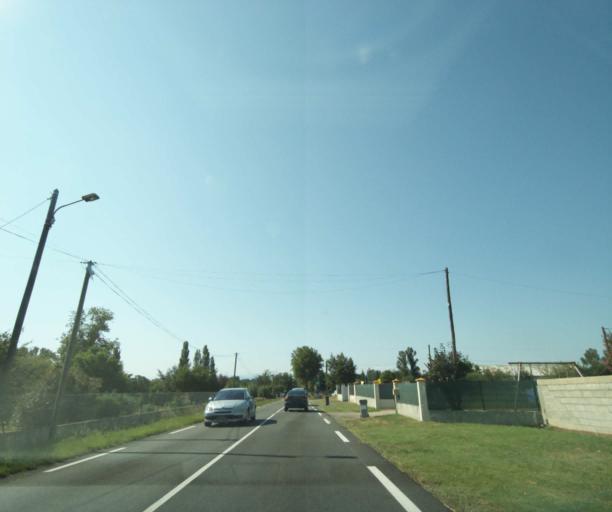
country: FR
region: Midi-Pyrenees
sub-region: Departement de la Haute-Garonne
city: Saint-Sulpice-sur-Leze
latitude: 43.3365
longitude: 1.3218
